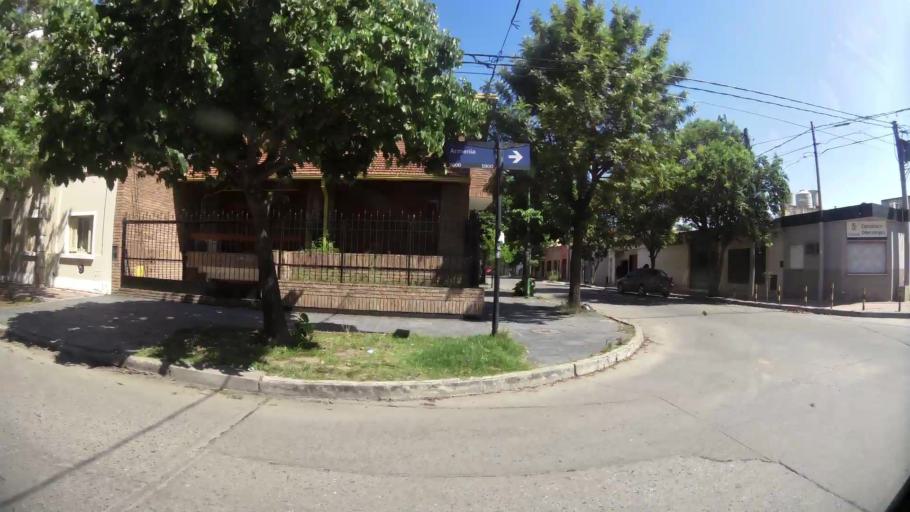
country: AR
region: Cordoba
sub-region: Departamento de Capital
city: Cordoba
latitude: -31.4044
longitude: -64.1610
